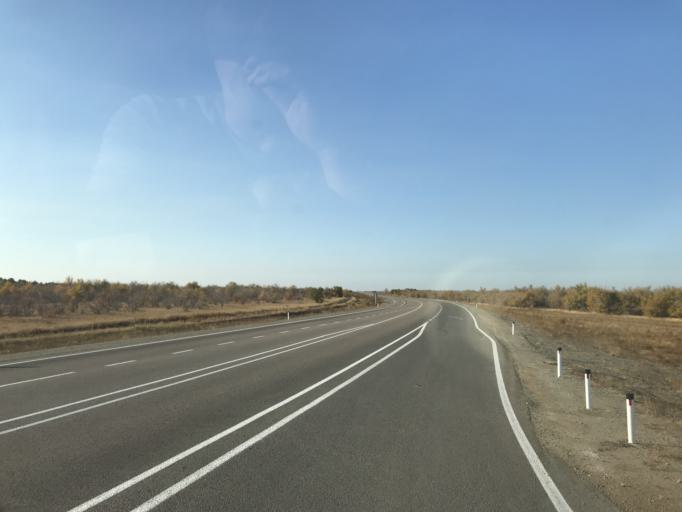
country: KZ
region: Pavlodar
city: Koktobe
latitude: 51.7286
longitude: 77.5593
